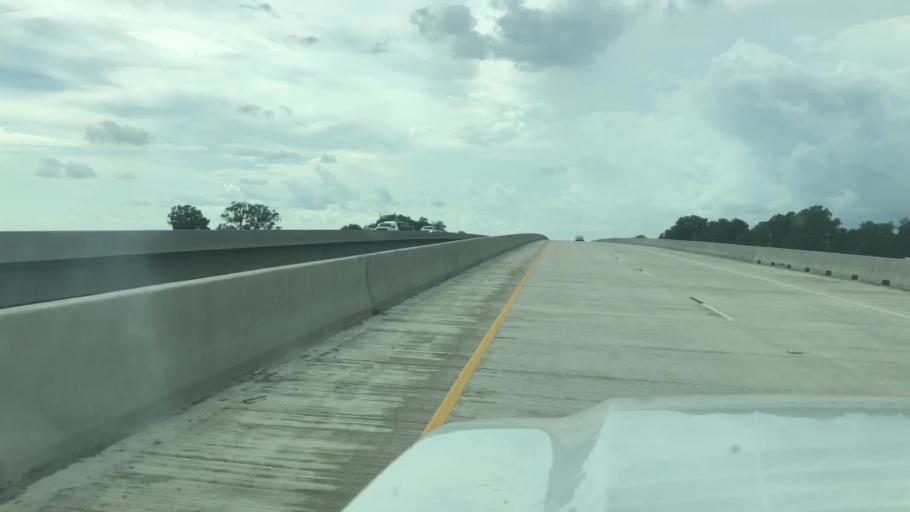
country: US
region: Louisiana
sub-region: Iberia Parish
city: Jeanerette
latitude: 29.8657
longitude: -91.6316
